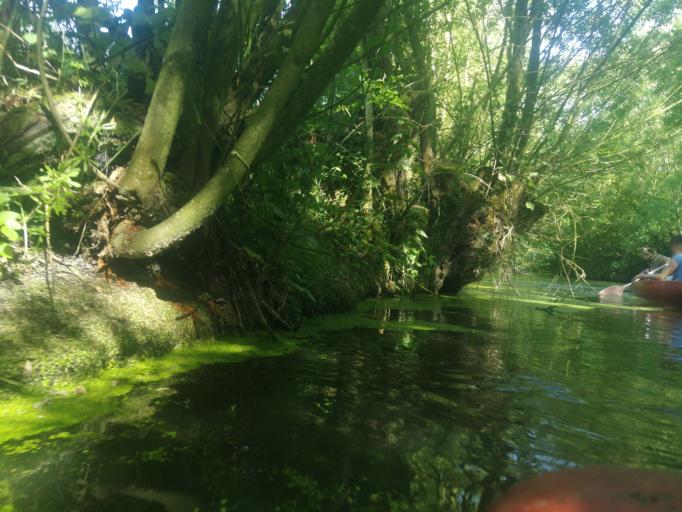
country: FR
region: Poitou-Charentes
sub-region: Departement de la Charente-Maritime
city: Marans
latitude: 46.3641
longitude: -0.9616
